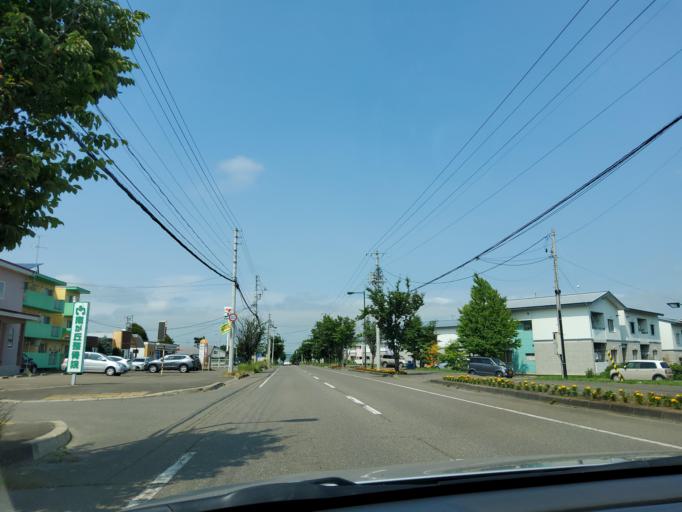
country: JP
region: Hokkaido
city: Obihiro
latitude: 42.9022
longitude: 143.0489
